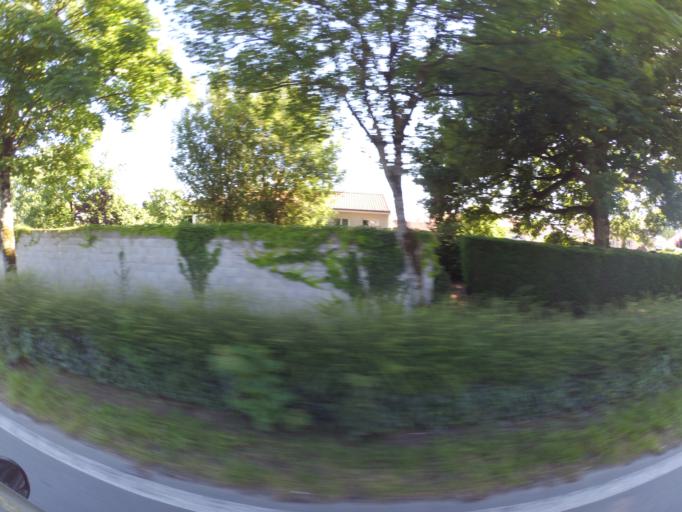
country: FR
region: Pays de la Loire
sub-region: Departement de la Vendee
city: Les Herbiers
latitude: 46.8596
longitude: -1.0169
